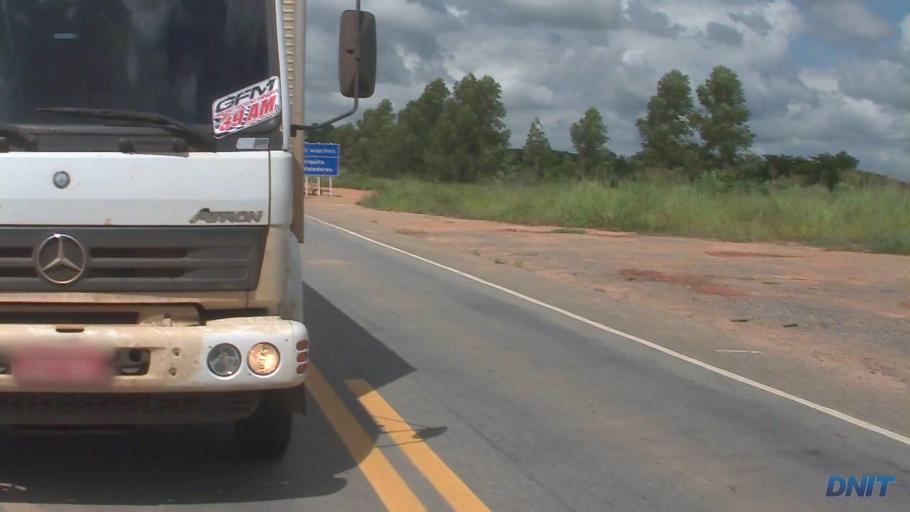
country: BR
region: Minas Gerais
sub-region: Governador Valadares
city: Governador Valadares
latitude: -19.0509
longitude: -42.1583
